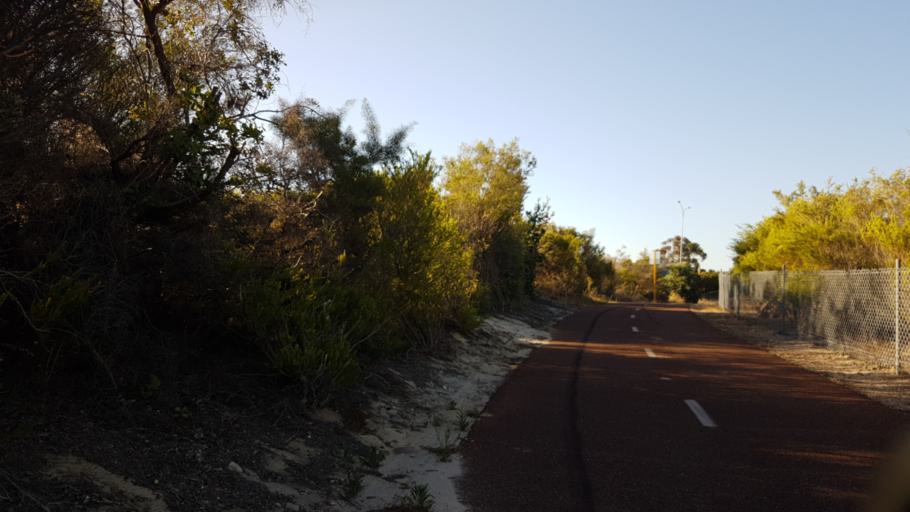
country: AU
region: Western Australia
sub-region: Kwinana
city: Bertram
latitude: -32.2324
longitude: 115.8492
